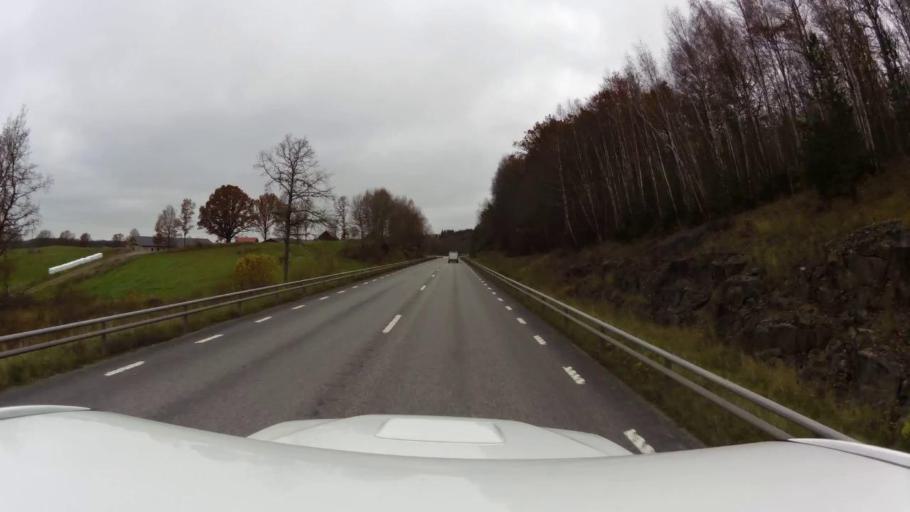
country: SE
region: OEstergoetland
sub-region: Kinda Kommun
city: Rimforsa
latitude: 58.1781
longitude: 15.6745
